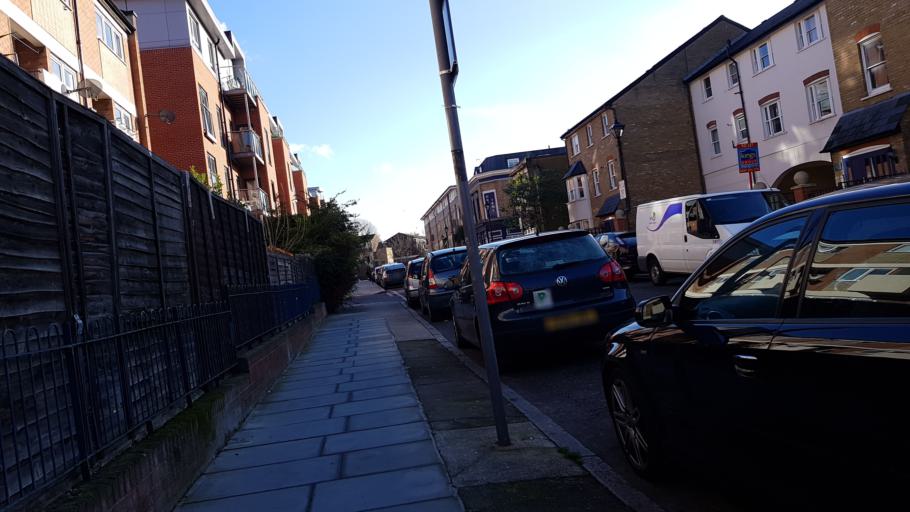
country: GB
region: England
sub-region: Greater London
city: Poplar
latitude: 51.5311
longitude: -0.0272
